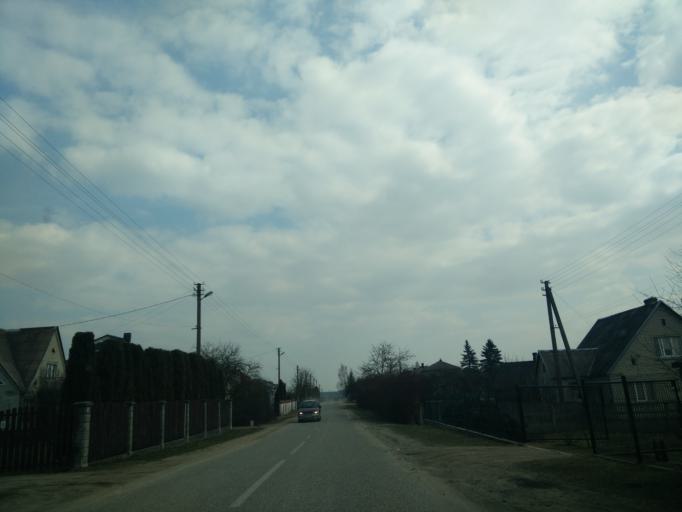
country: LT
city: Trakai
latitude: 54.6106
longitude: 24.9847
